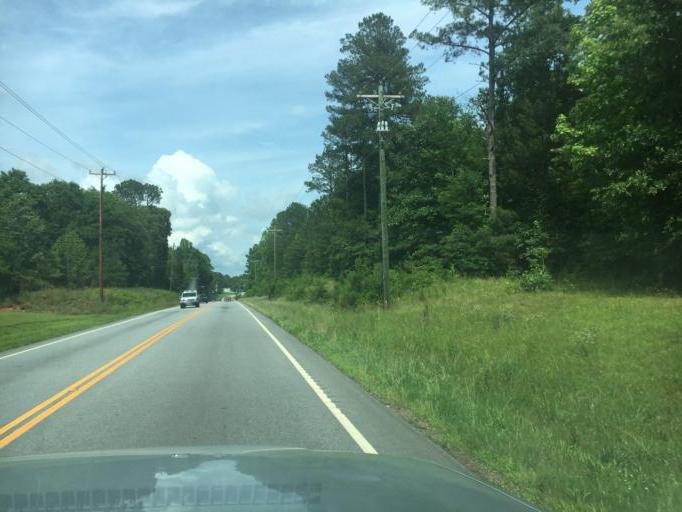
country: US
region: South Carolina
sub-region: Greenville County
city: Fountain Inn
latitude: 34.6718
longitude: -82.2365
